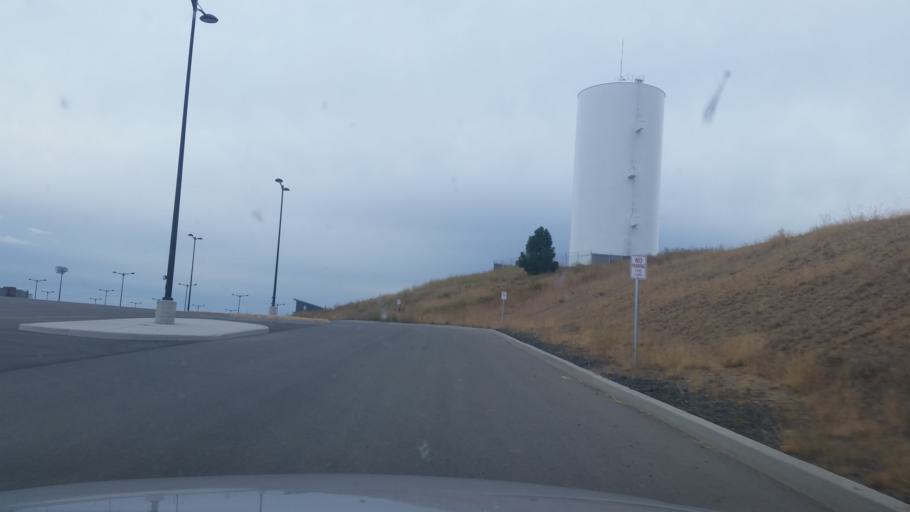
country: US
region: Washington
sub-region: Spokane County
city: Cheney
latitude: 47.4946
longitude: -117.5918
